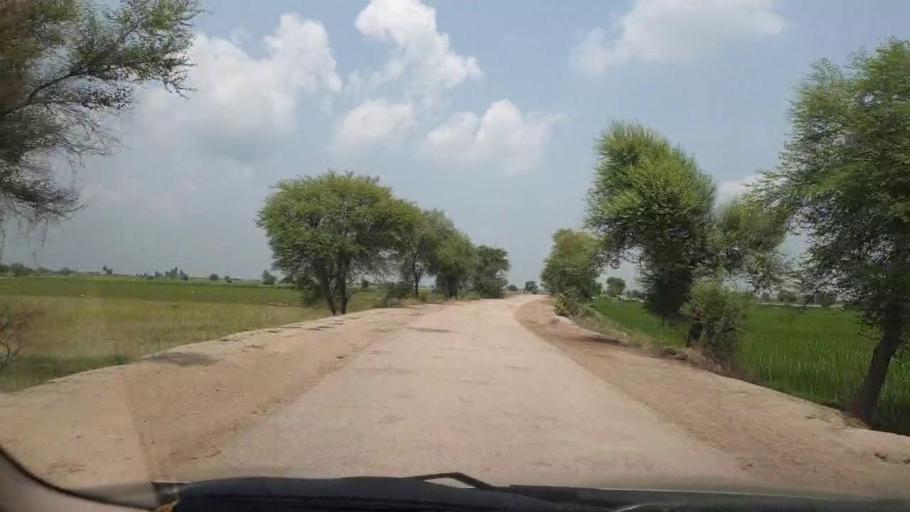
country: PK
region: Sindh
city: Larkana
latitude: 27.6065
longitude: 68.1438
